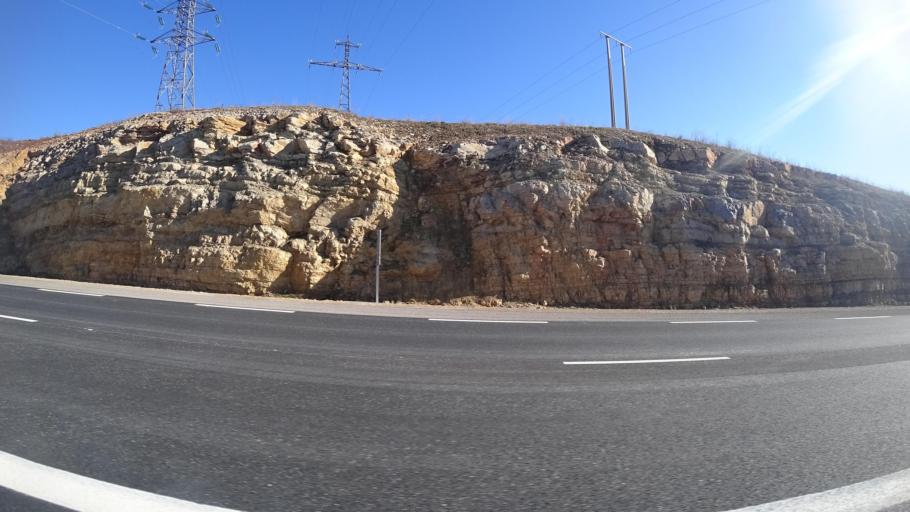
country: FR
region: Midi-Pyrenees
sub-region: Departement de l'Aveyron
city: Sebazac-Concoures
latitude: 44.3891
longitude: 2.6137
